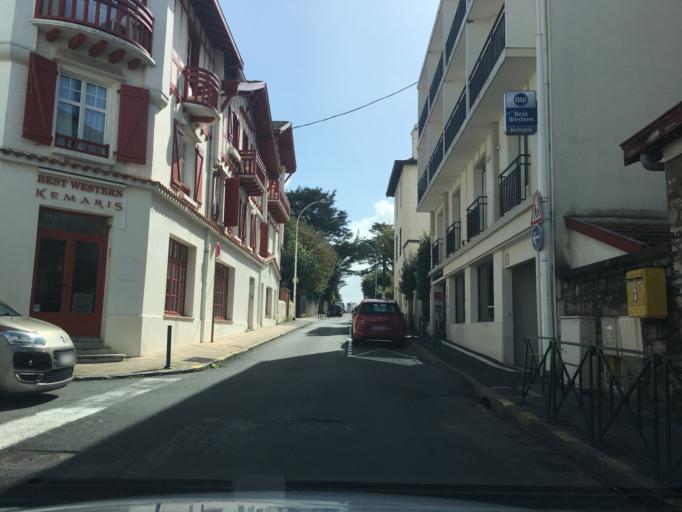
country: FR
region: Aquitaine
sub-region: Departement des Pyrenees-Atlantiques
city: Biarritz
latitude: 43.4768
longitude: -1.5624
